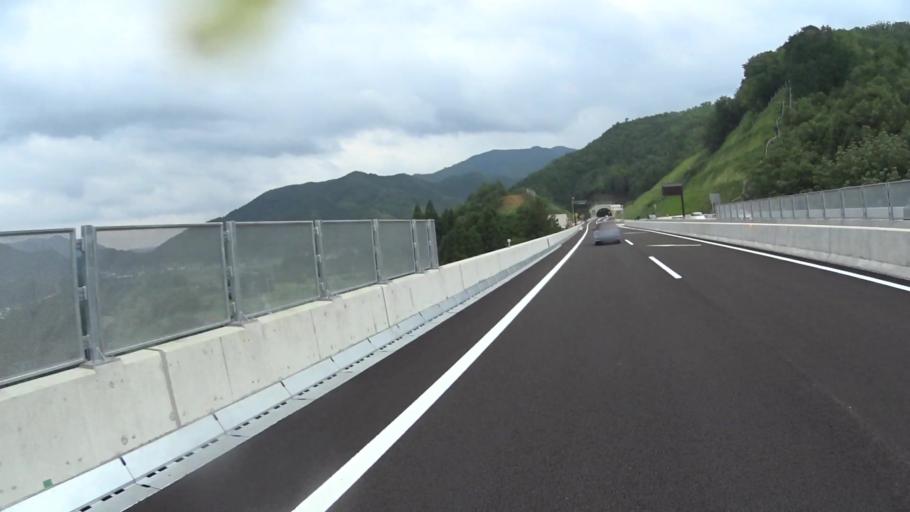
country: JP
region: Kyoto
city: Ayabe
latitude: 35.2732
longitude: 135.3409
